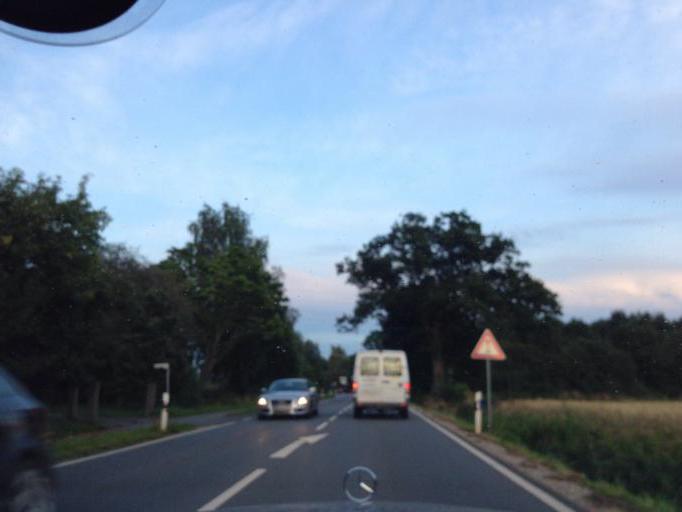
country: DE
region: Schleswig-Holstein
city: Bargteheide
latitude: 53.7173
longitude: 10.2862
